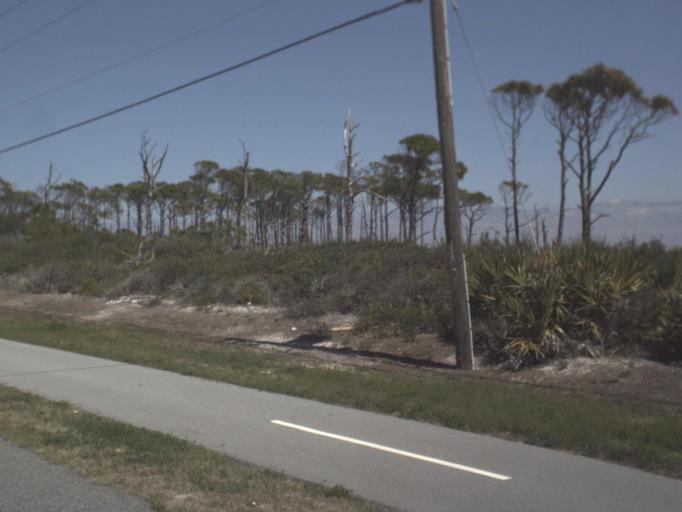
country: US
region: Florida
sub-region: Gulf County
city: Port Saint Joe
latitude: 29.6894
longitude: -85.3721
